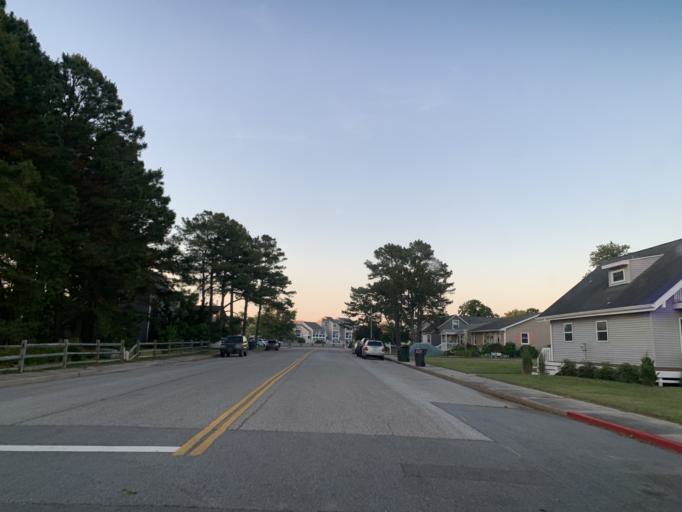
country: US
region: Delaware
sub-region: Sussex County
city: Bethany Beach
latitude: 38.4499
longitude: -75.0608
